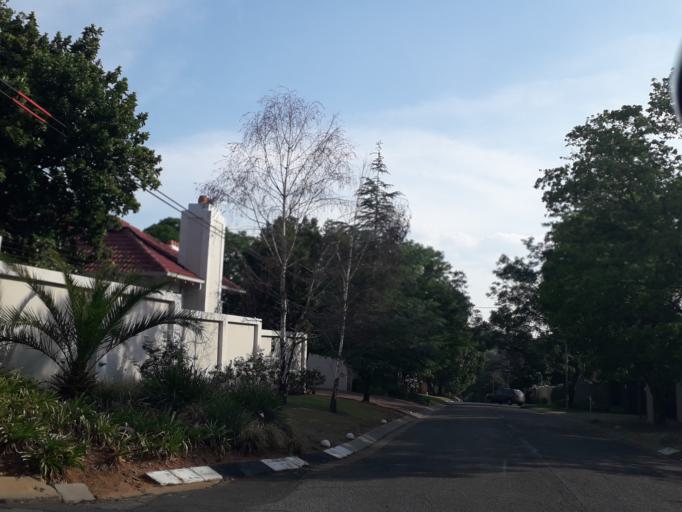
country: ZA
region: Gauteng
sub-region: City of Johannesburg Metropolitan Municipality
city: Johannesburg
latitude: -26.0980
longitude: 28.0433
